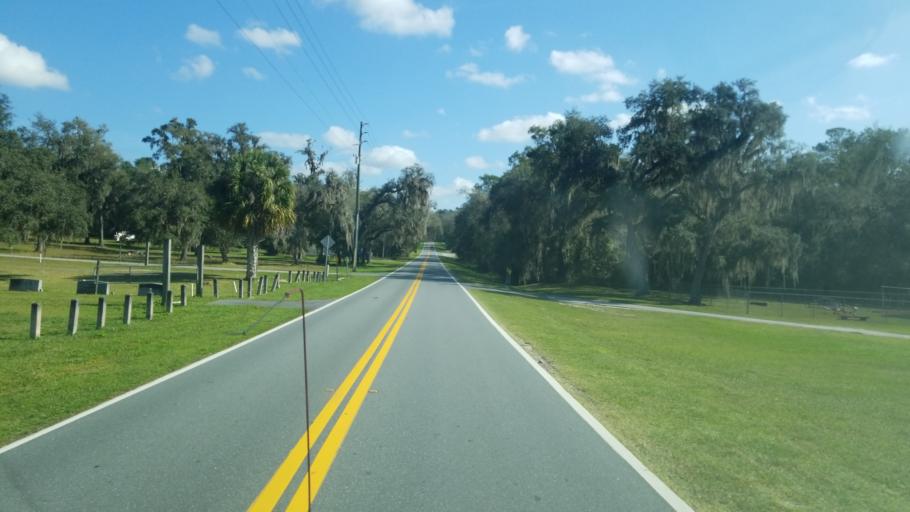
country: US
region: Florida
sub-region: Hernando County
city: North Brooksville
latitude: 28.6349
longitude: -82.3665
